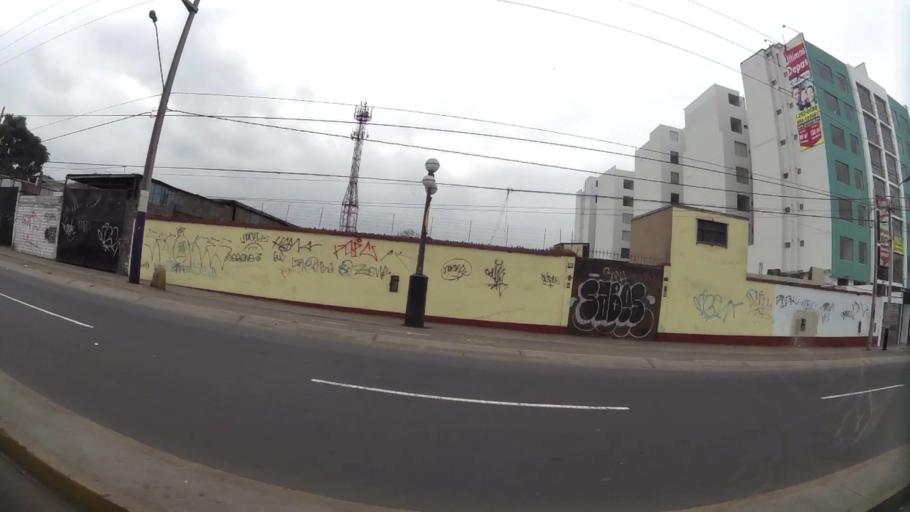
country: PE
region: Lima
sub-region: Lima
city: Surco
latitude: -12.1827
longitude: -77.0078
